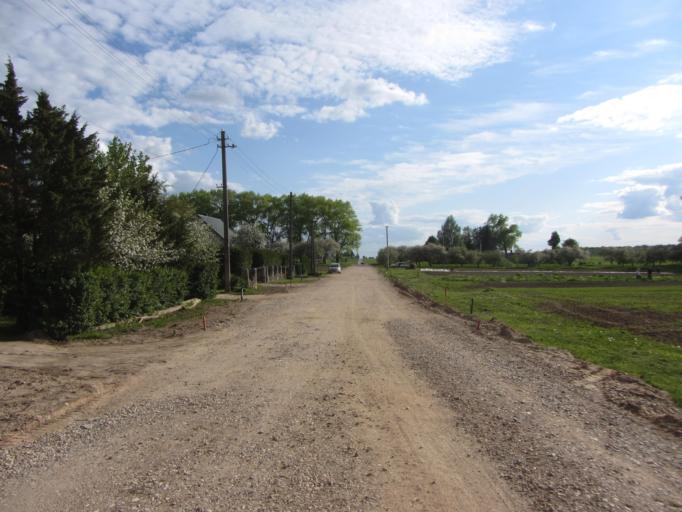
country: LT
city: Sirvintos
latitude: 55.0498
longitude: 24.9371
